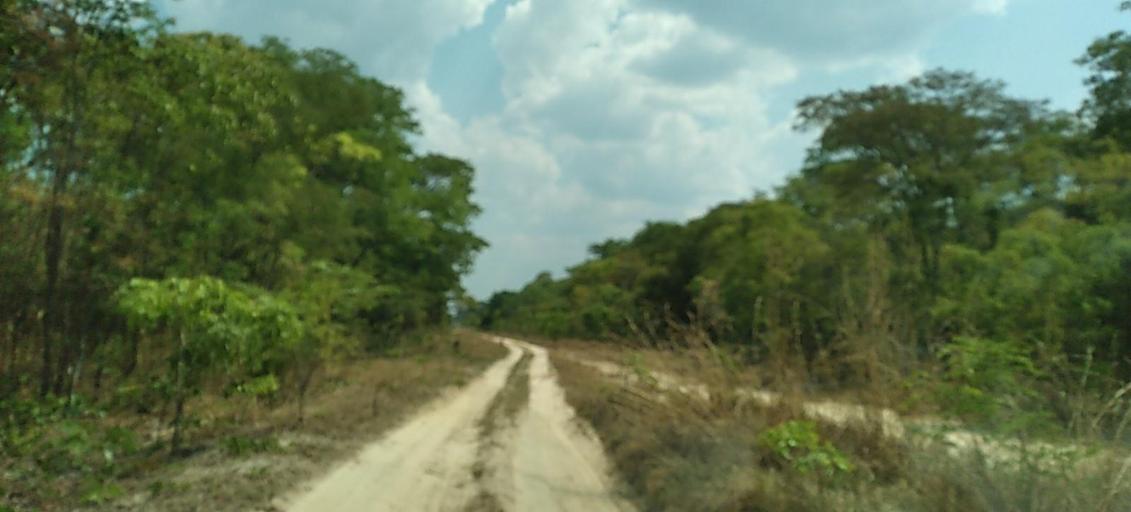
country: ZM
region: Copperbelt
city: Mpongwe
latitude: -13.8293
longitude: 27.9405
